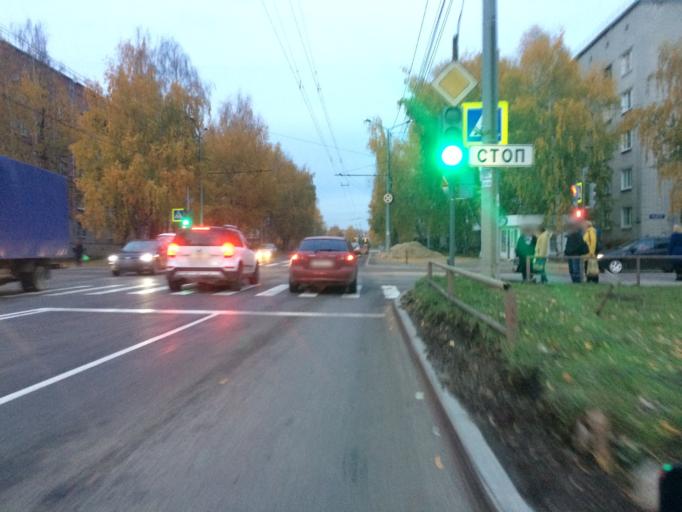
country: RU
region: Mariy-El
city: Yoshkar-Ola
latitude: 56.6164
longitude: 47.8840
